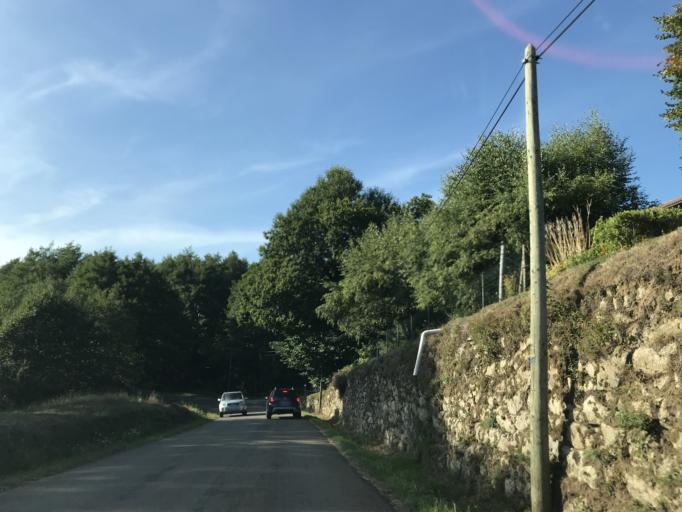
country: FR
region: Auvergne
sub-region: Departement du Puy-de-Dome
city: Job
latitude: 45.7091
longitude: 3.7201
